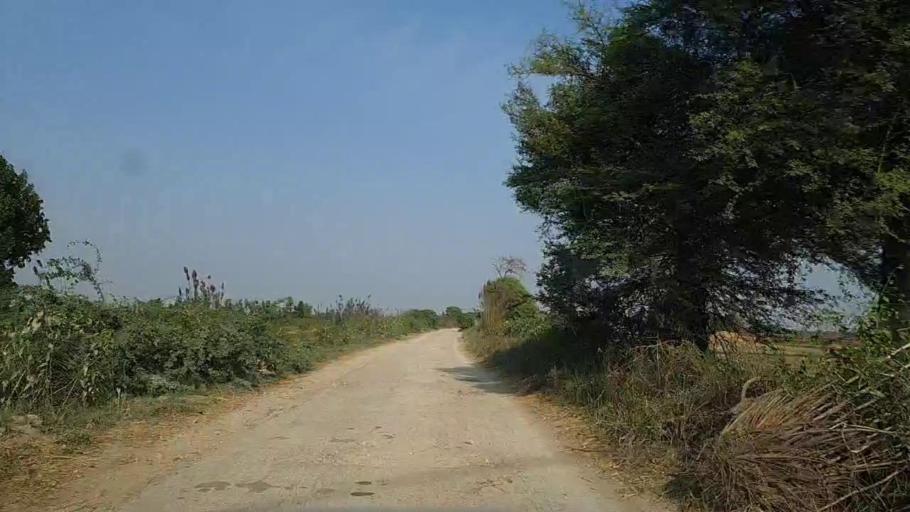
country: PK
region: Sindh
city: Mirpur Sakro
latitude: 24.5946
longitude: 67.5806
